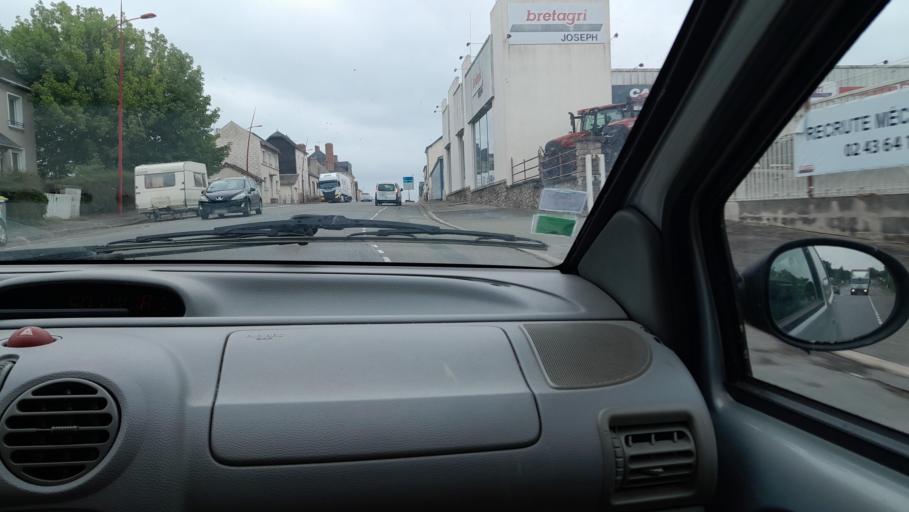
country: FR
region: Pays de la Loire
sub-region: Departement de la Mayenne
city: Cosse-le-Vivien
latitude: 47.9421
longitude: -0.9142
